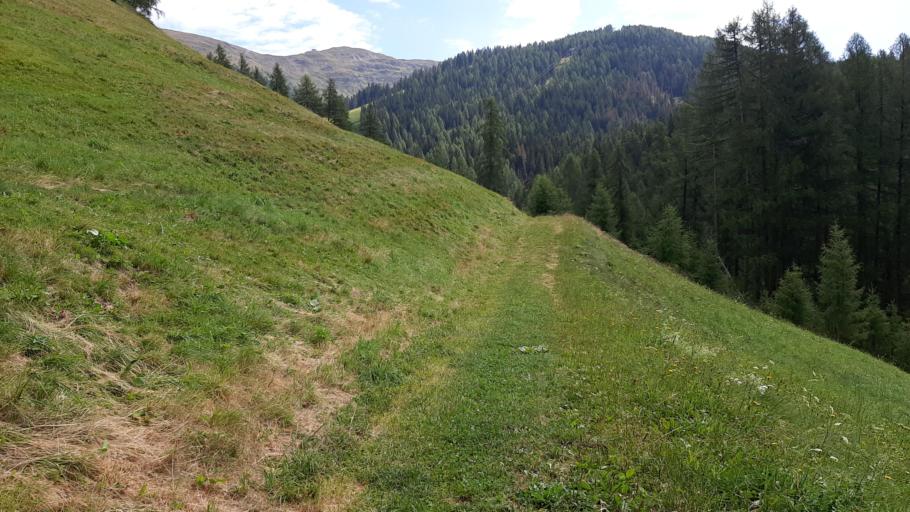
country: IT
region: Trentino-Alto Adige
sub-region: Bolzano
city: Sesto
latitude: 46.6962
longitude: 12.3748
